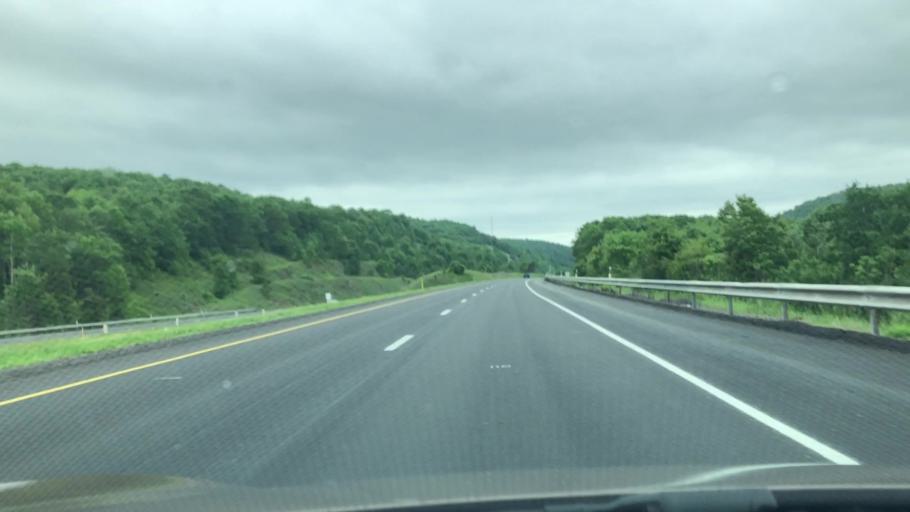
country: US
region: Pennsylvania
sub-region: Centre County
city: Milesburg
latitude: 41.0148
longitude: -77.8827
